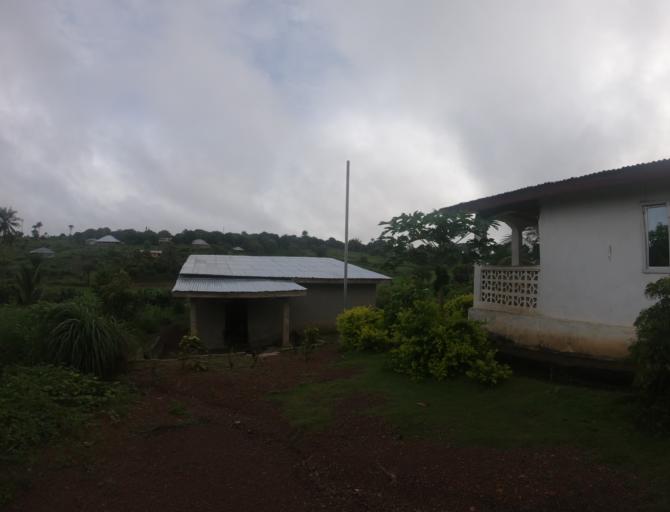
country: SL
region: Southern Province
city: Rotifunk
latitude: 8.4894
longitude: -12.7618
